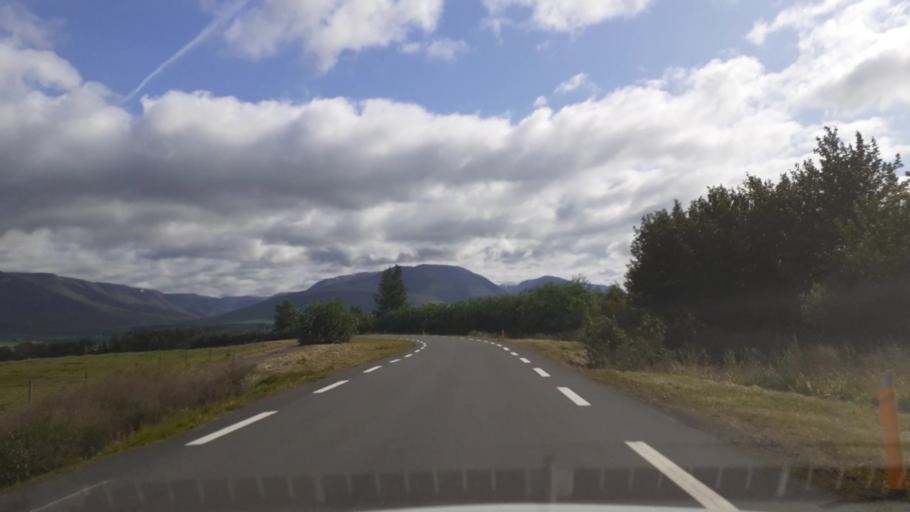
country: IS
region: Northeast
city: Akureyri
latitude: 65.6504
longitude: -18.0919
